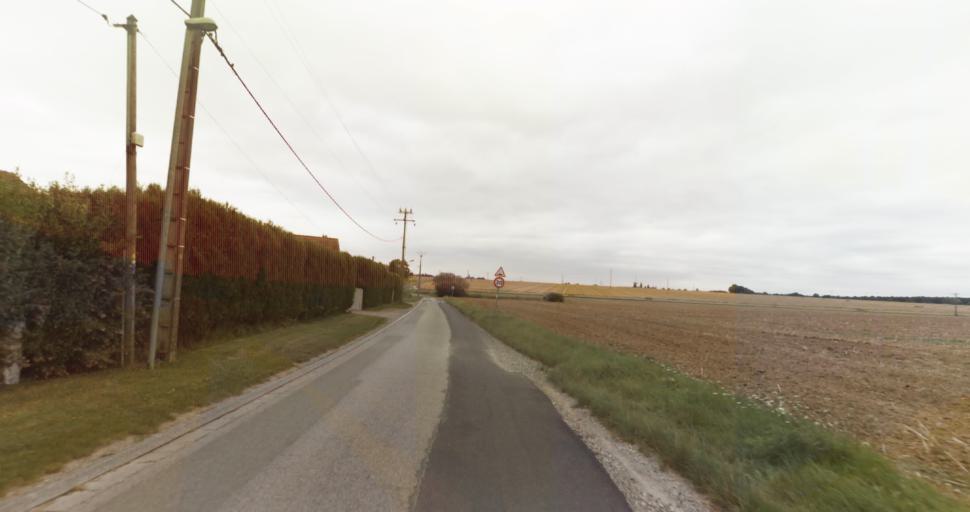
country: FR
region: Haute-Normandie
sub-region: Departement de l'Eure
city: La Couture-Boussey
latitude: 48.9110
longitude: 1.4071
